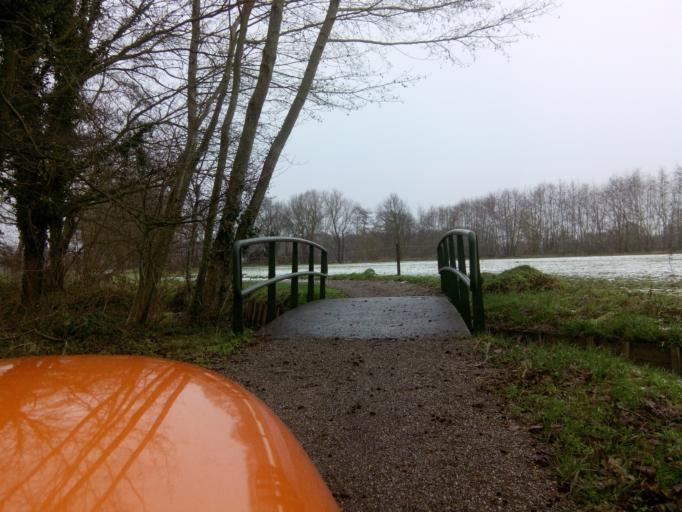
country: NL
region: Gelderland
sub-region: Gemeente Nijkerk
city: Nijkerk
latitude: 52.2256
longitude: 5.5266
